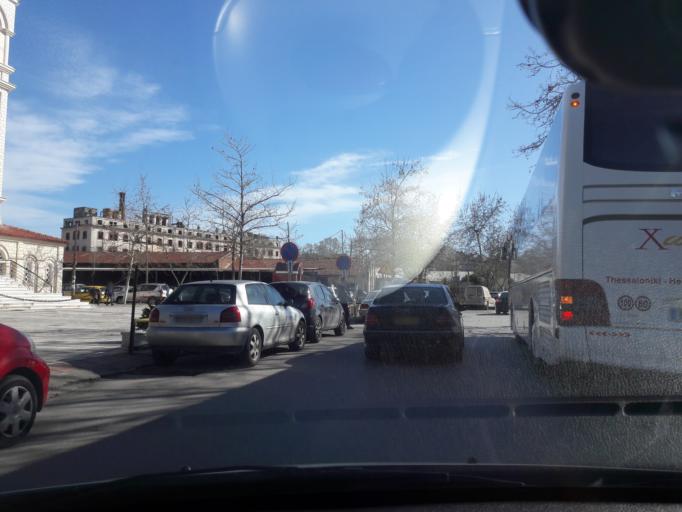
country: GR
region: Central Macedonia
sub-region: Nomos Thessalonikis
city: Kalamaria
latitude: 40.5981
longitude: 22.9507
